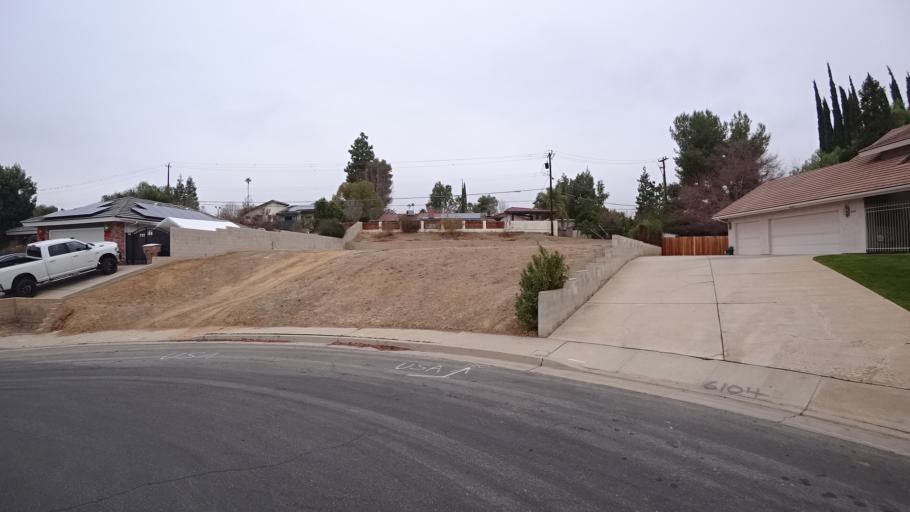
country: US
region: California
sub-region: Kern County
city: Bakersfield
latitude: 35.3861
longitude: -118.9345
